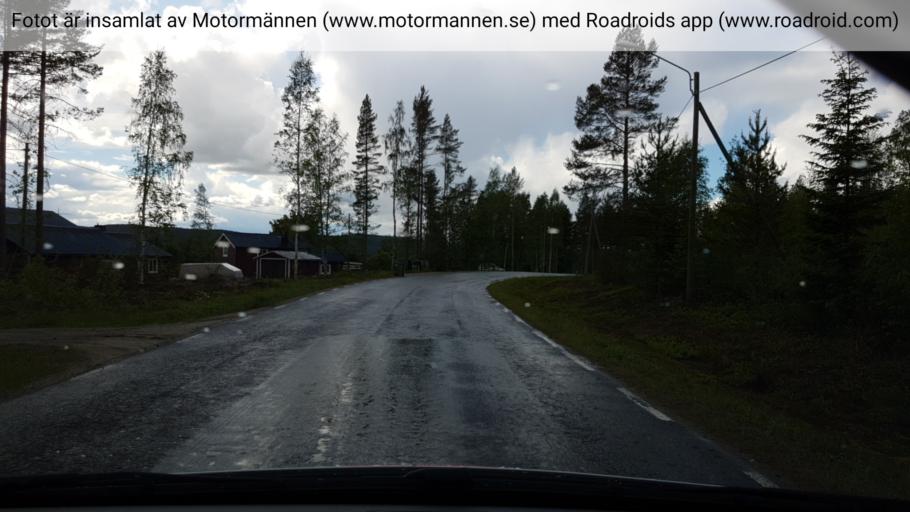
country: SE
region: Vaesterbotten
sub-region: Umea Kommun
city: Roback
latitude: 63.9957
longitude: 20.1036
